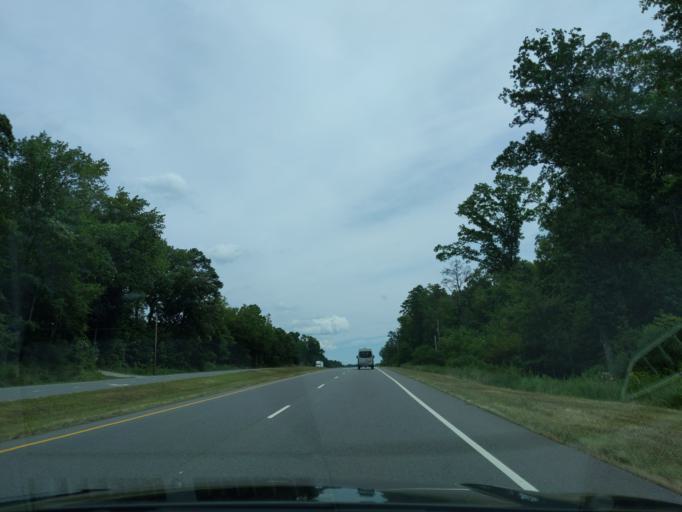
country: US
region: North Carolina
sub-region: Cabarrus County
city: Mount Pleasant
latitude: 35.3996
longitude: -80.4694
